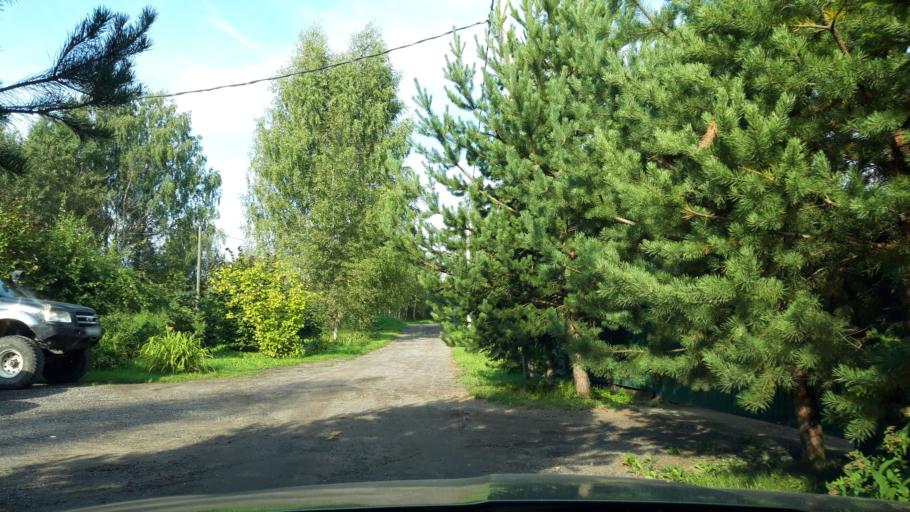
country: RU
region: Moskovskaya
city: Radumlya
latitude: 56.0566
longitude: 37.1541
